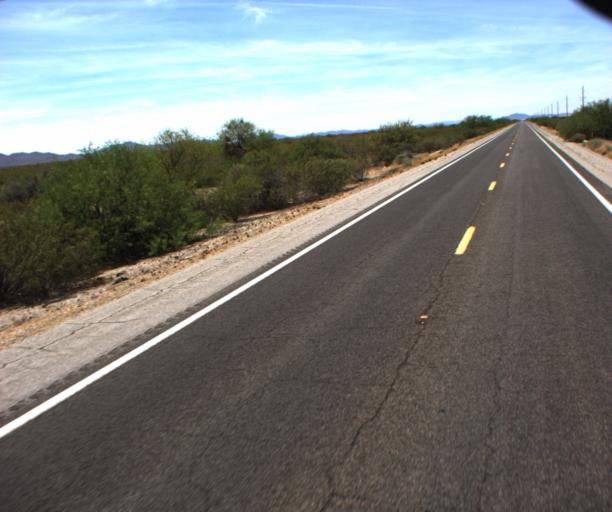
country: US
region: Arizona
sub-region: La Paz County
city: Salome
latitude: 33.8562
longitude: -113.4337
